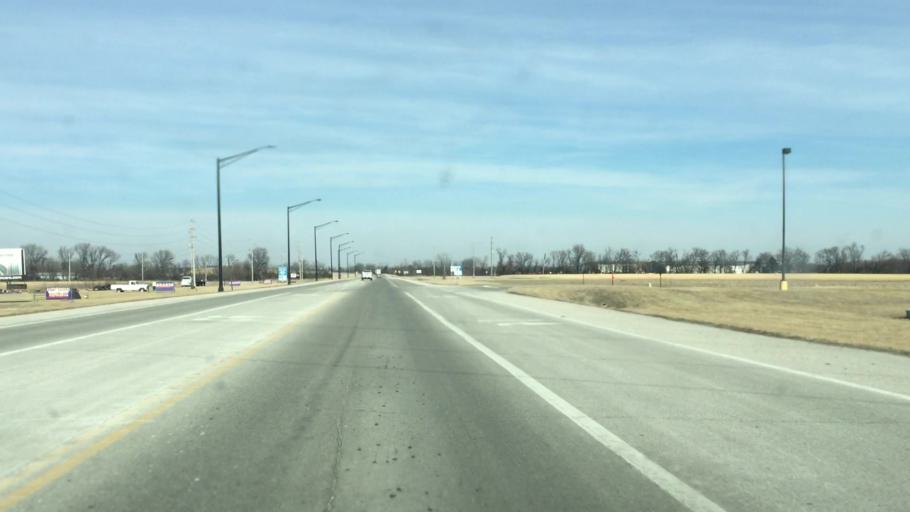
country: US
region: Kansas
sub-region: Labette County
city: Parsons
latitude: 37.3722
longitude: -95.2584
